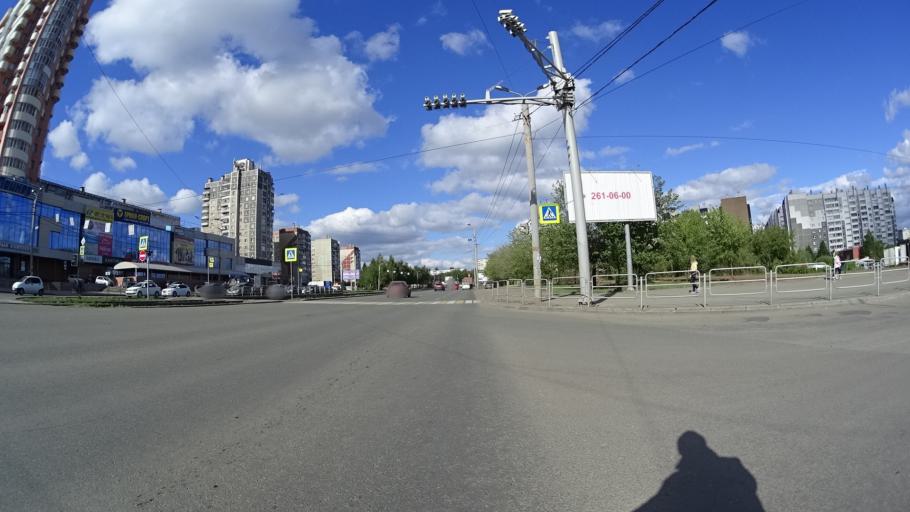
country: RU
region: Chelyabinsk
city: Roshchino
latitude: 55.1858
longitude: 61.2996
